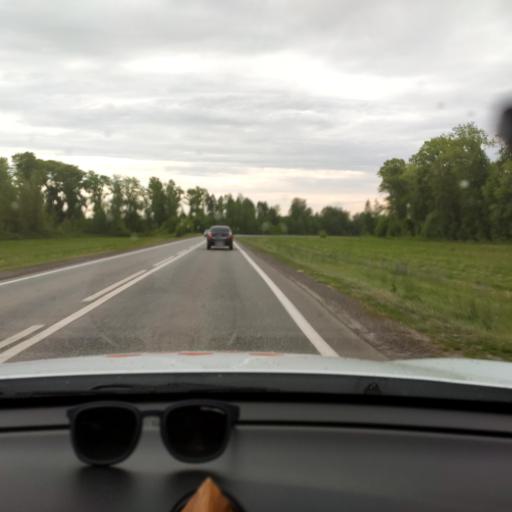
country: RU
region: Tatarstan
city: Pestretsy
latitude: 55.8360
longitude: 49.6442
